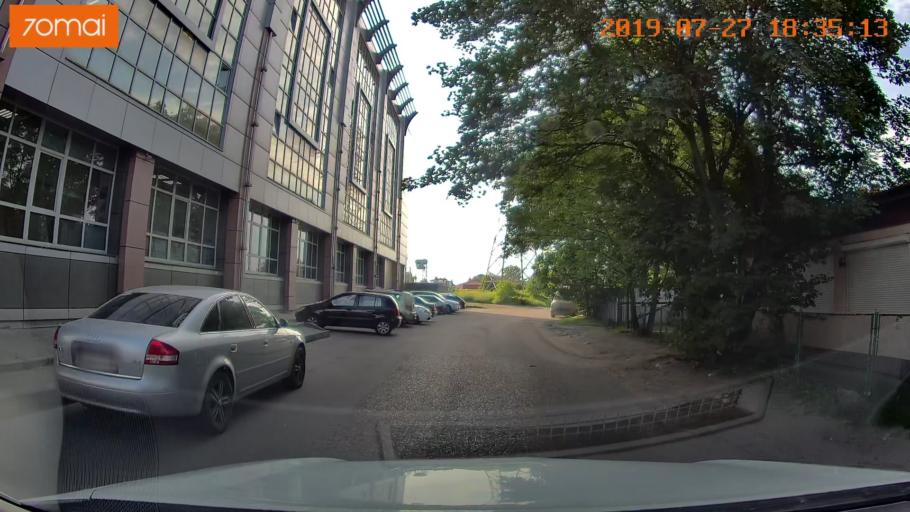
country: RU
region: Kaliningrad
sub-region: Gorod Kaliningrad
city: Kaliningrad
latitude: 54.7034
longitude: 20.4993
